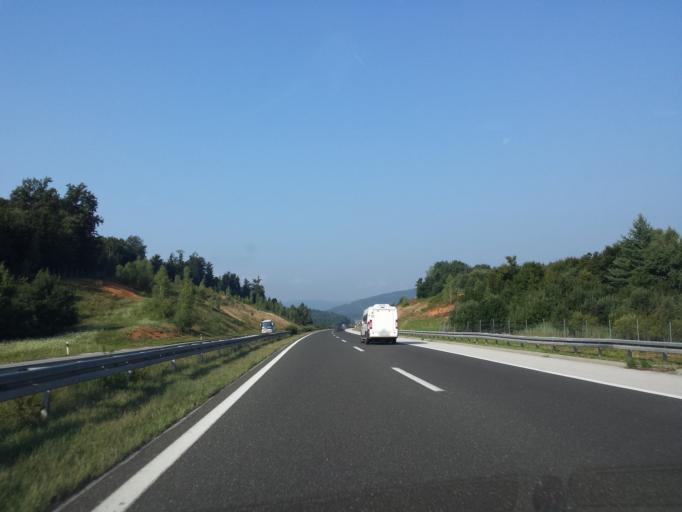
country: HR
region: Karlovacka
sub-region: Grad Ogulin
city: Ogulin
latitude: 45.4317
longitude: 15.3212
